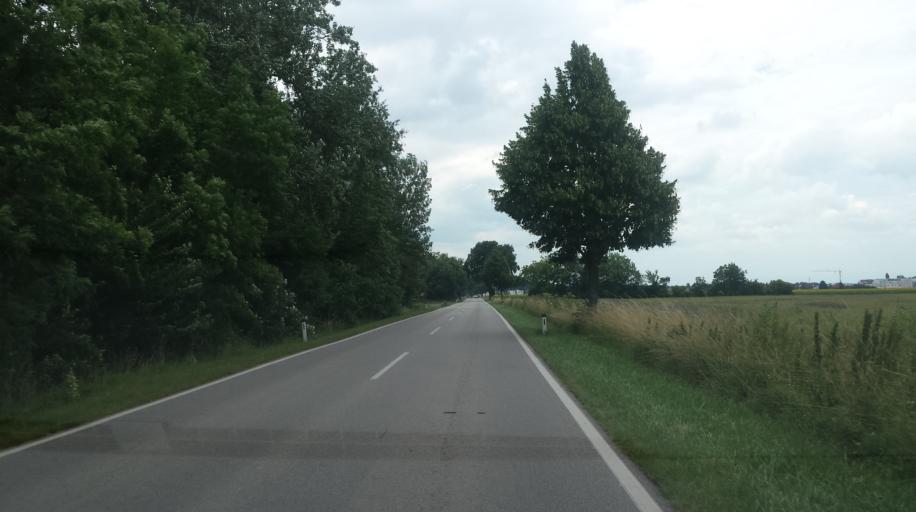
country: AT
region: Lower Austria
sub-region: Politischer Bezirk Baden
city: Mitterndorf an der Fischa
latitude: 47.9735
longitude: 16.4332
